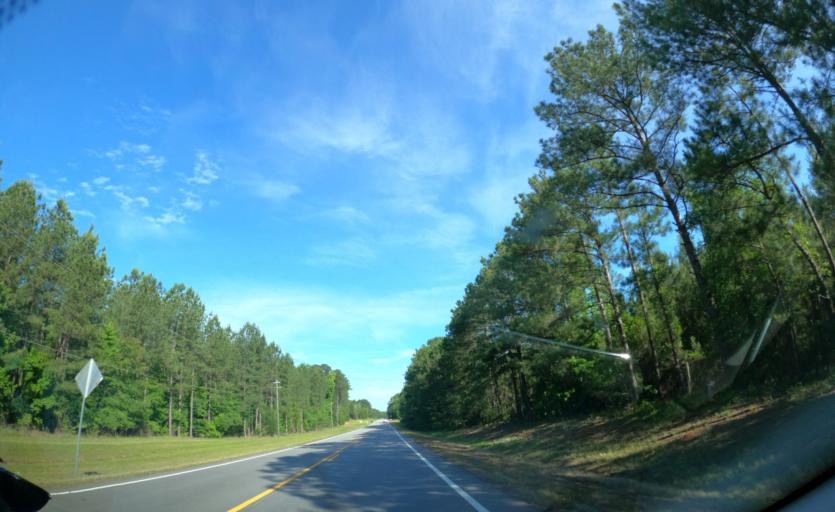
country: US
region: Georgia
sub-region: Columbia County
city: Appling
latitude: 33.6308
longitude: -82.2928
